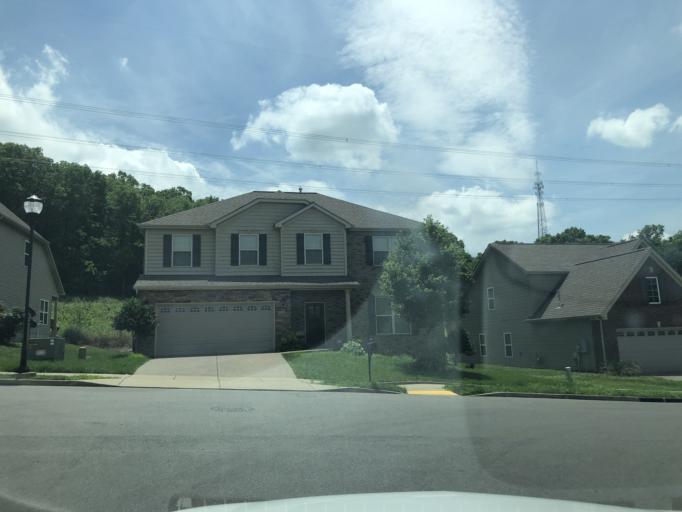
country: US
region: Tennessee
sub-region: Rutherford County
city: La Vergne
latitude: 36.0239
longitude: -86.6384
